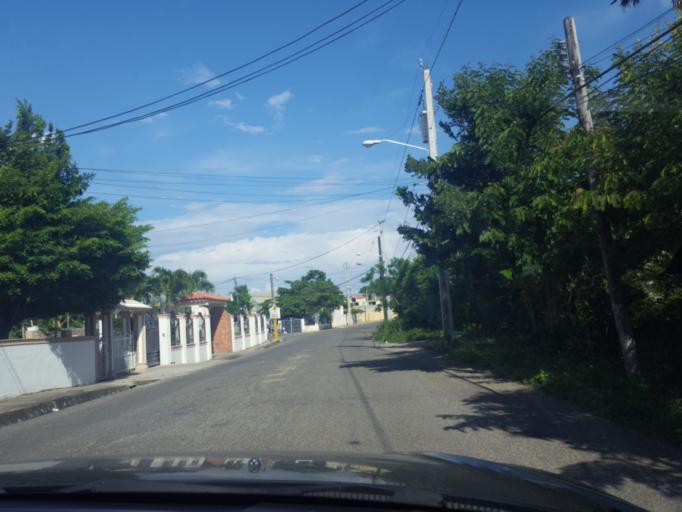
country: DO
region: La Vega
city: Rio Verde Arriba
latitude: 19.3676
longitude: -70.6062
